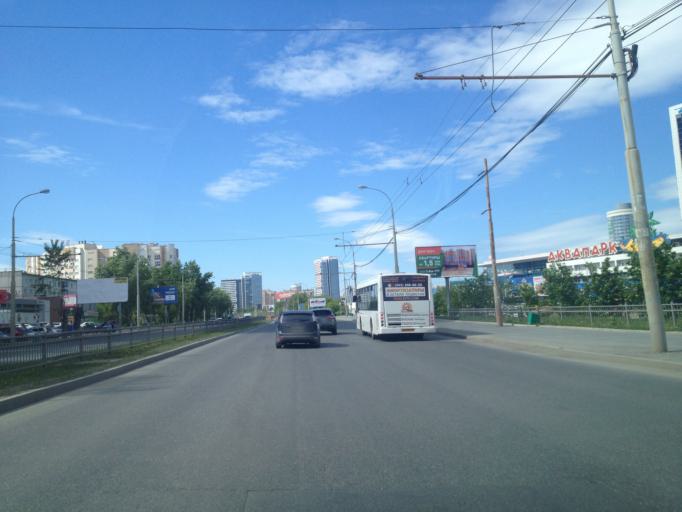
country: RU
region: Sverdlovsk
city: Yekaterinburg
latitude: 56.7888
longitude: 60.6467
